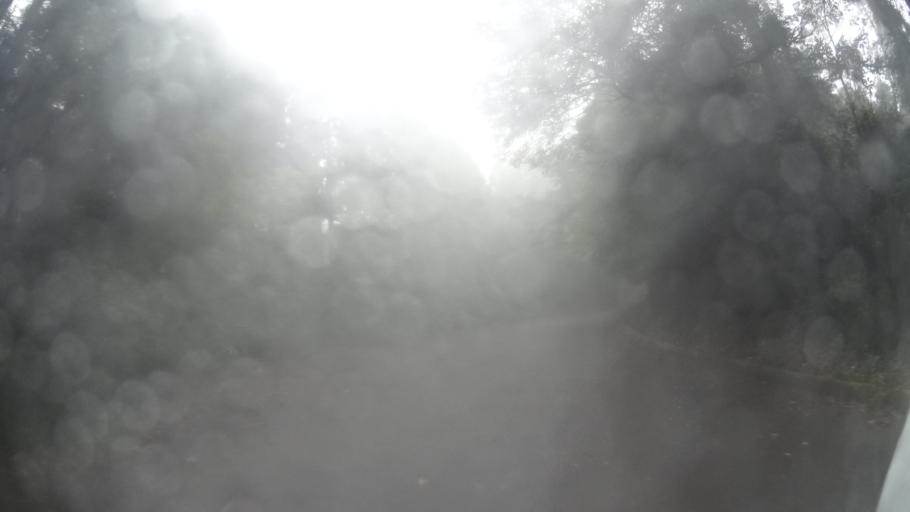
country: JP
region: Kagoshima
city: Nishinoomote
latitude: 30.2970
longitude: 130.5666
